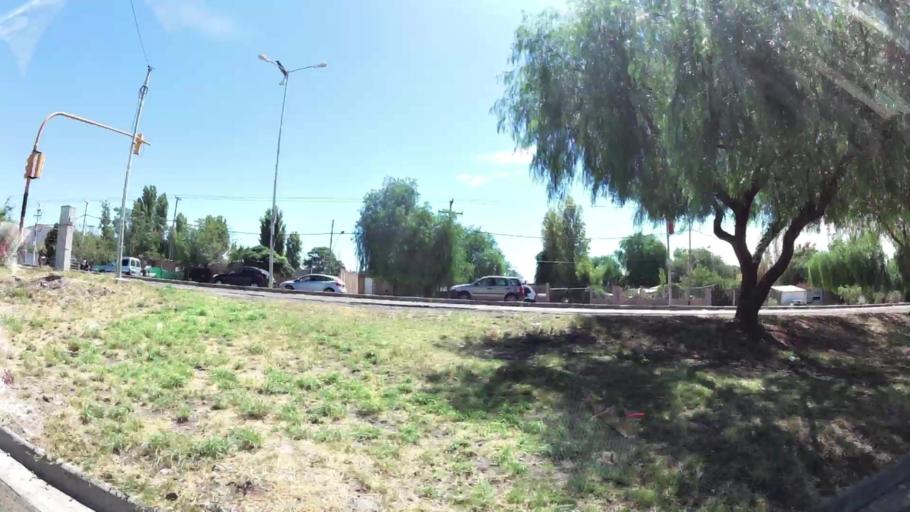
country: AR
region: Mendoza
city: Las Heras
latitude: -32.8543
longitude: -68.8709
